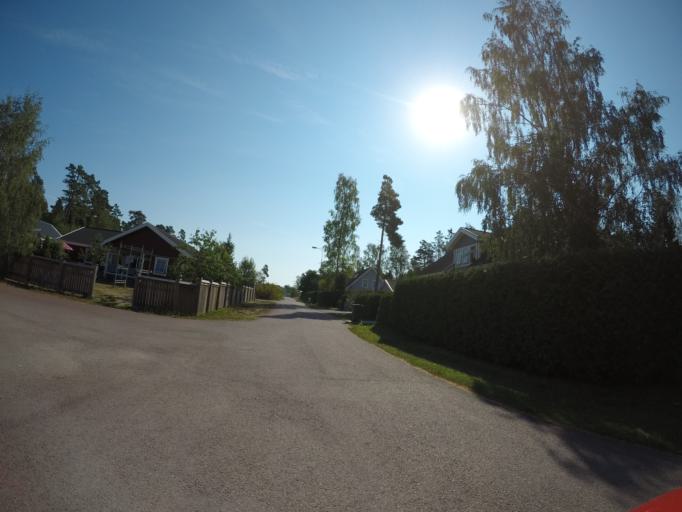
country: AX
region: Alands landsbygd
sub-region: Finstroem
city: Finstroem
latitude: 60.2288
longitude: 19.9769
